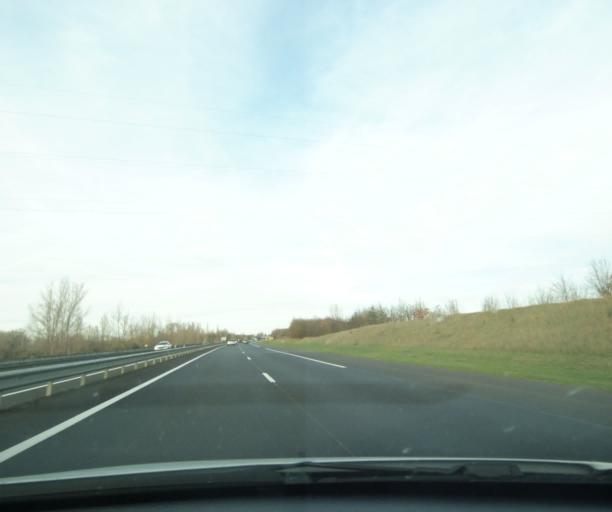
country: FR
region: Midi-Pyrenees
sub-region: Departement de la Haute-Garonne
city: Frouzins
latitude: 43.4963
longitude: 1.3366
